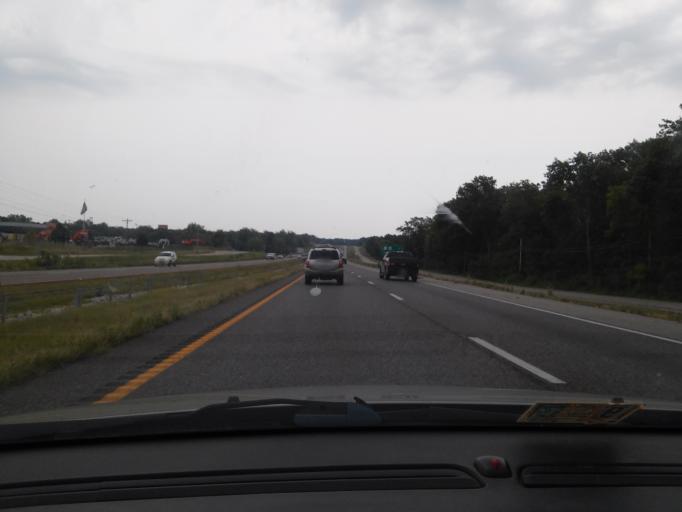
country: US
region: Missouri
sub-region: Boone County
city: Columbia
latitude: 38.9587
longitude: -92.1911
